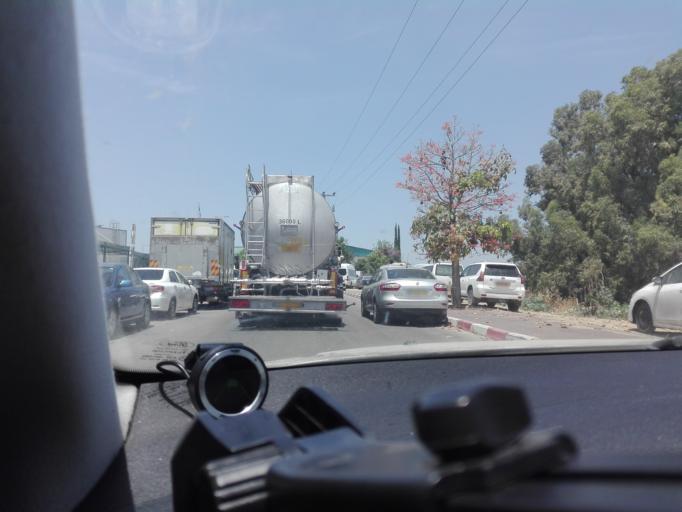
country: IL
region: Central District
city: Bene 'Ayish
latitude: 31.7395
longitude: 34.7496
